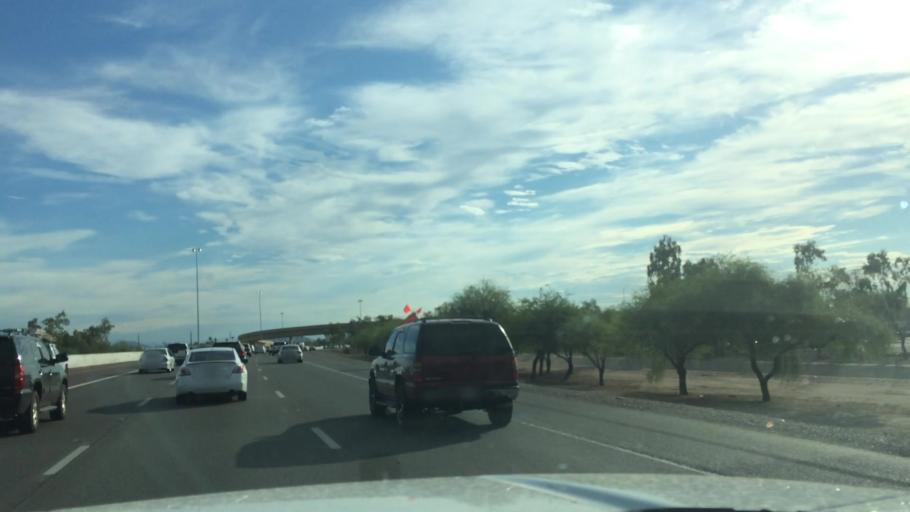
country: US
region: Arizona
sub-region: Maricopa County
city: Sun City
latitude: 33.5979
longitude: -112.2589
